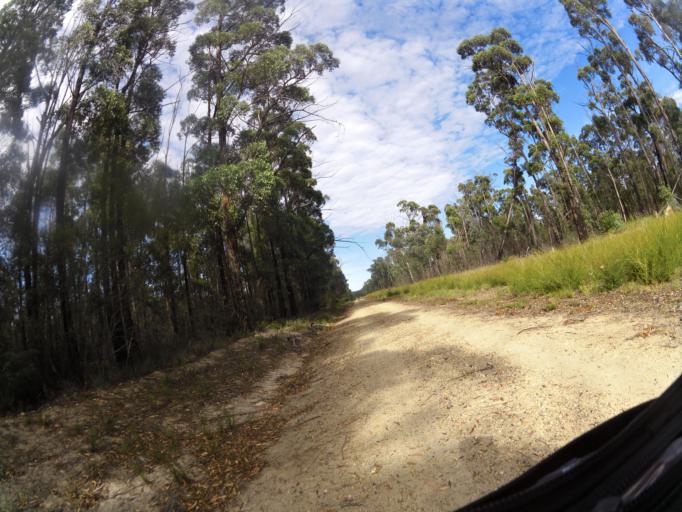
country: AU
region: Victoria
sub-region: East Gippsland
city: Lakes Entrance
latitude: -37.7463
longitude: 148.2356
